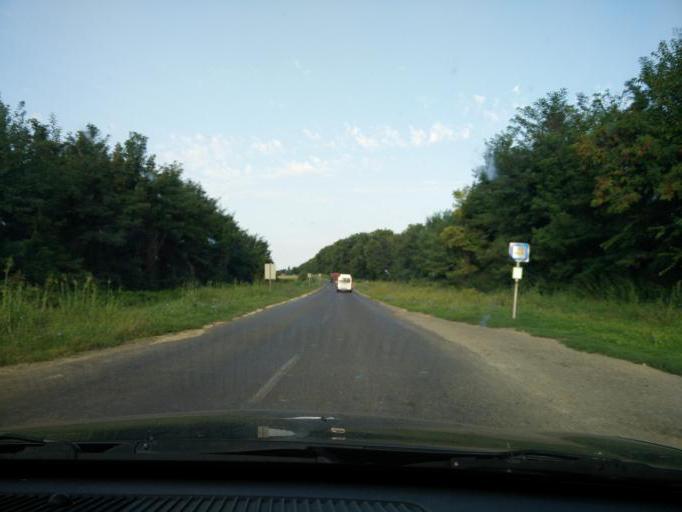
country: HU
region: Tolna
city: Nagymanyok
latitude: 46.2816
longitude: 18.4366
